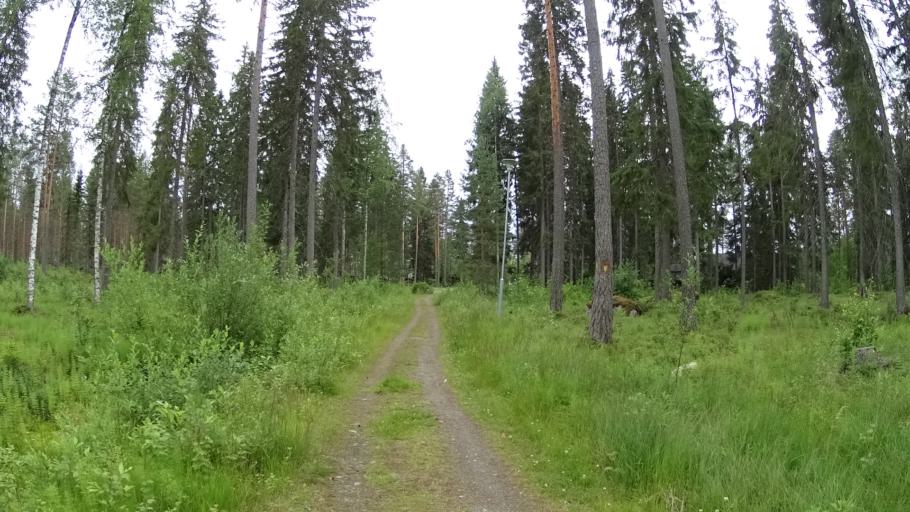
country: FI
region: Southern Ostrobothnia
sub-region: Kuusiokunnat
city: AEhtaeri
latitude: 62.5291
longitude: 24.1934
